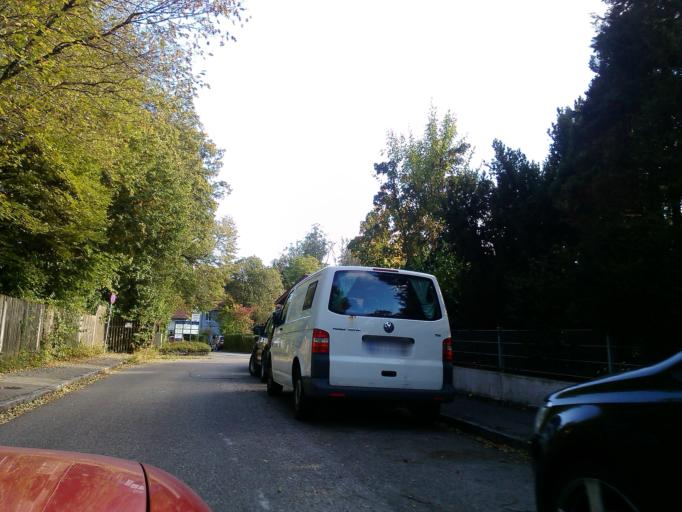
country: DE
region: Bavaria
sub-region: Upper Bavaria
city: Gauting
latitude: 48.0590
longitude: 11.3775
